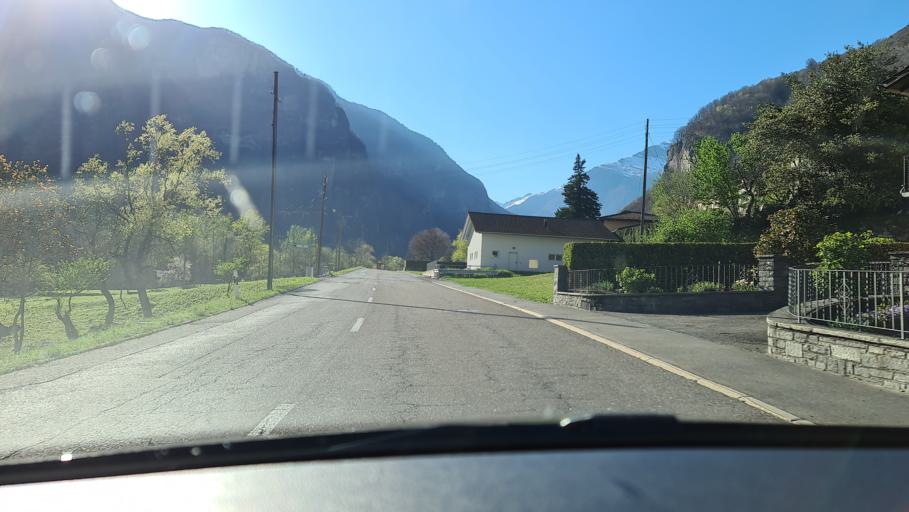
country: CH
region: Ticino
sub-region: Vallemaggia District
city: Cevio
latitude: 46.2862
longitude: 8.6647
